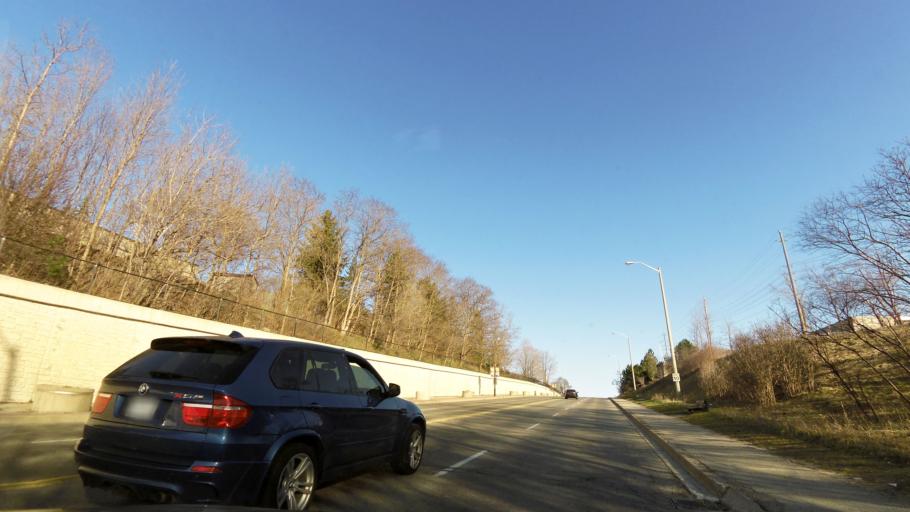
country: CA
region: Ontario
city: Brampton
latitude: 43.8777
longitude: -79.7357
